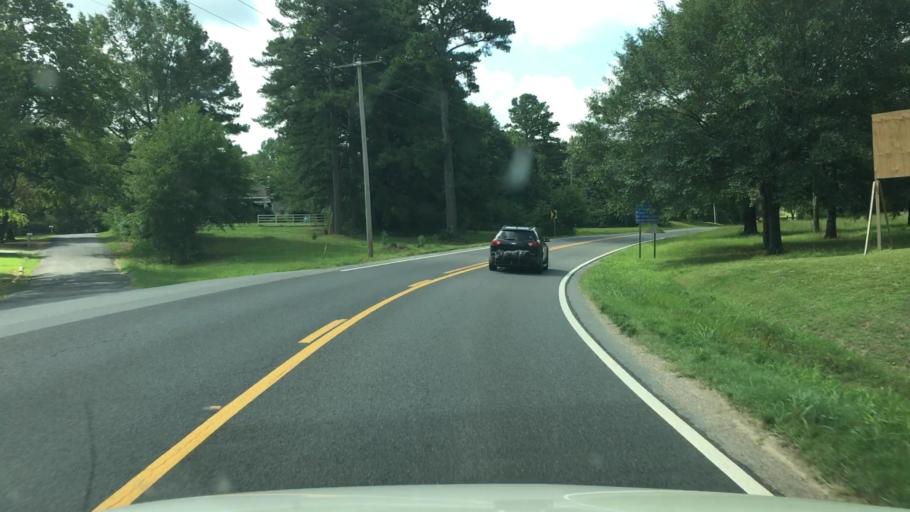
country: US
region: Arkansas
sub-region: Garland County
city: Lake Hamilton
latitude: 34.2949
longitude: -93.1624
